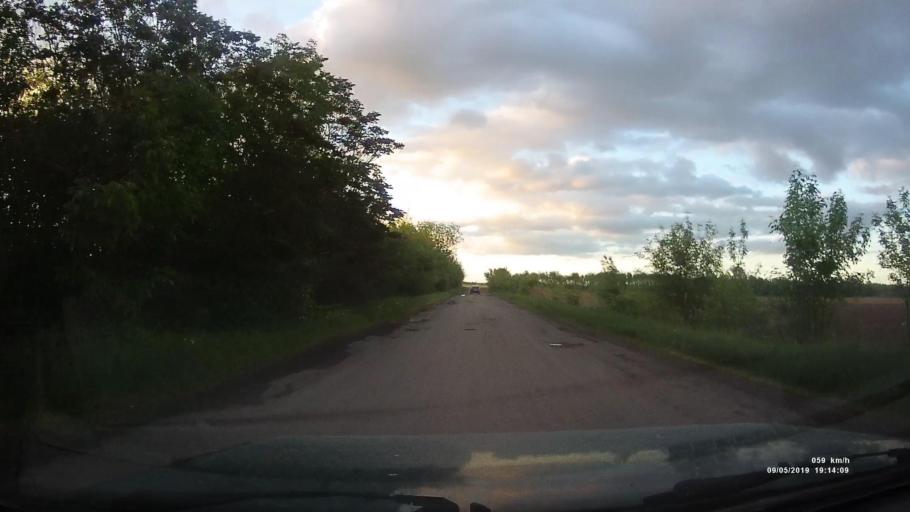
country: RU
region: Krasnodarskiy
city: Kanelovskaya
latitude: 46.7558
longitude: 39.2140
